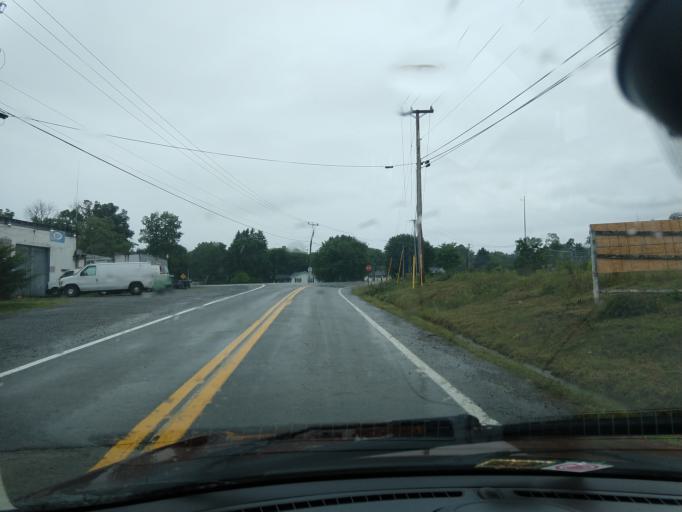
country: US
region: West Virginia
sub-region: Mercer County
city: Athens
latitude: 37.3624
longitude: -81.0380
